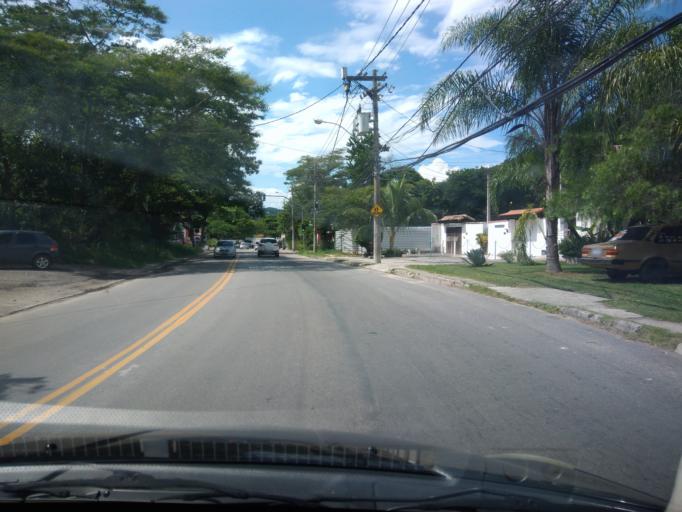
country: BR
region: Rio de Janeiro
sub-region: Niteroi
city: Niteroi
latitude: -22.9518
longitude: -43.0251
